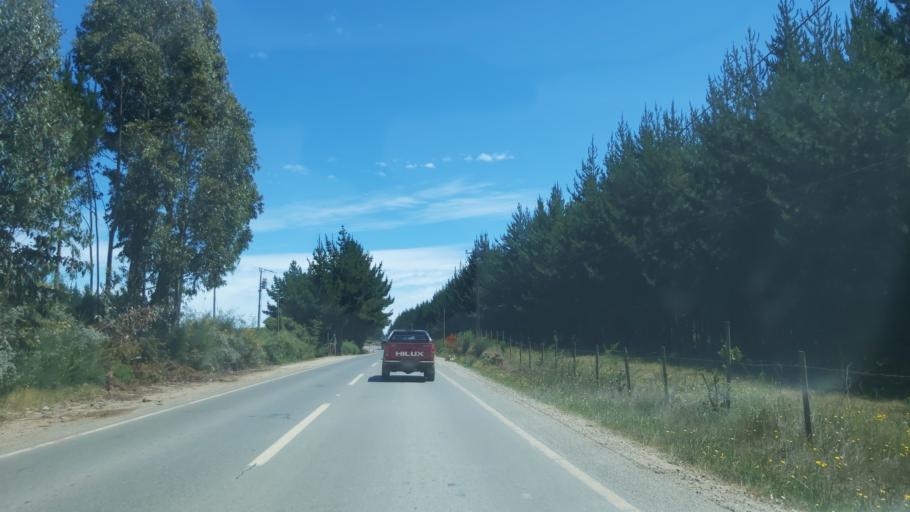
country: CL
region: Maule
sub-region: Provincia de Talca
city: Constitucion
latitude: -35.3935
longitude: -72.4273
